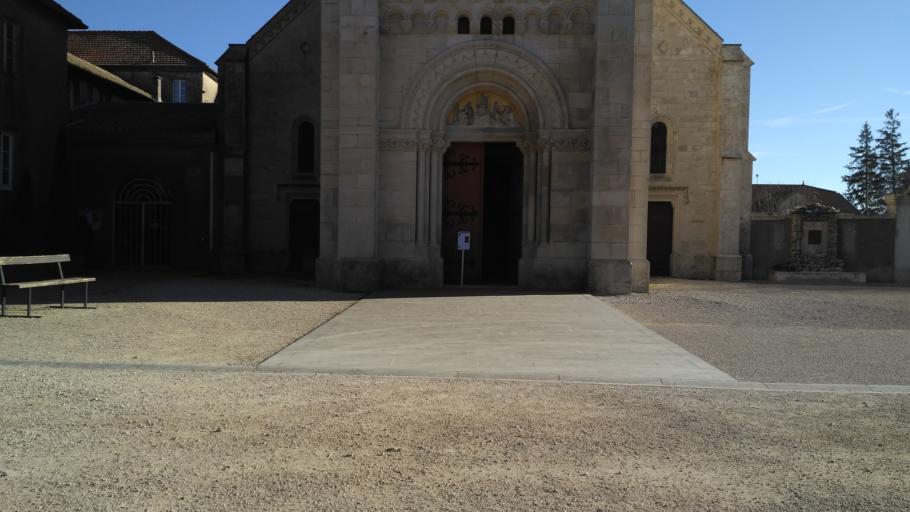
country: FR
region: Lorraine
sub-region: Departement de Meurthe-et-Moselle
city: Vezelise
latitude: 48.4310
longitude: 6.0835
